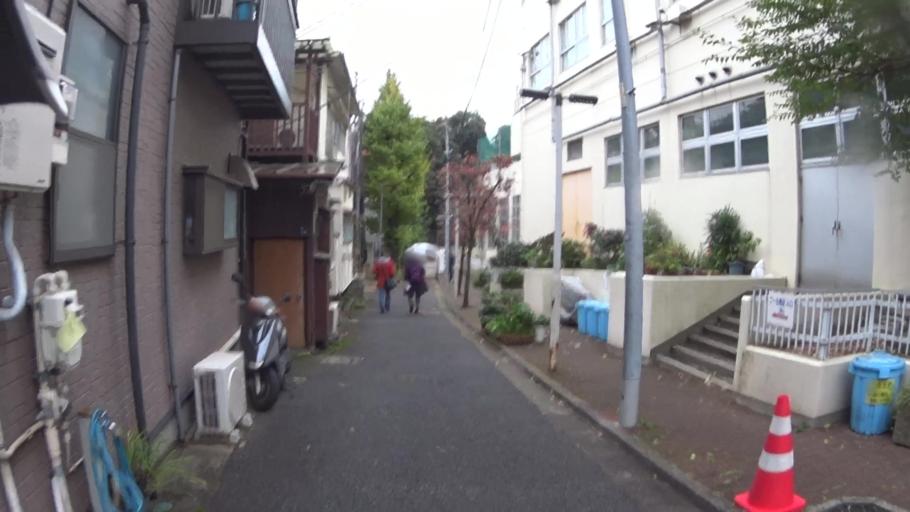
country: JP
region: Tokyo
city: Tokyo
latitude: 35.6499
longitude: 139.7304
